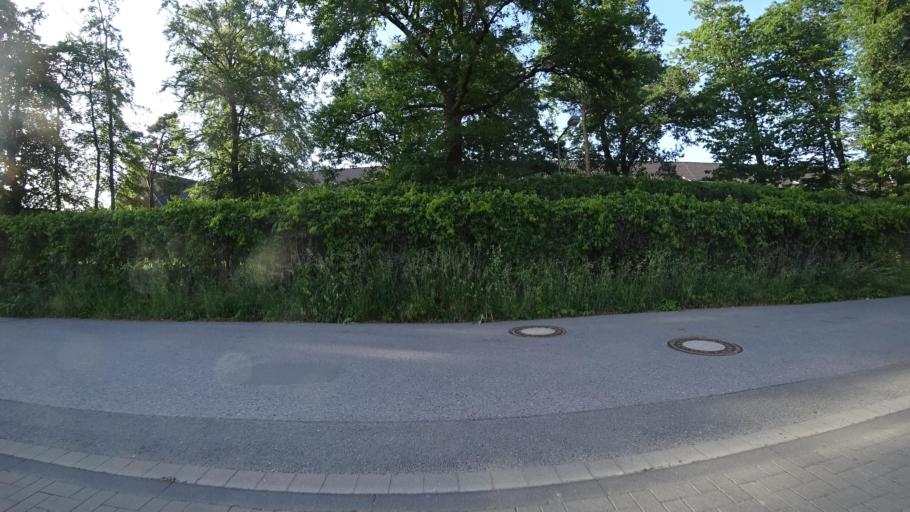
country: DE
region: North Rhine-Westphalia
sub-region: Regierungsbezirk Detmold
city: Guetersloh
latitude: 51.8950
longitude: 8.4124
